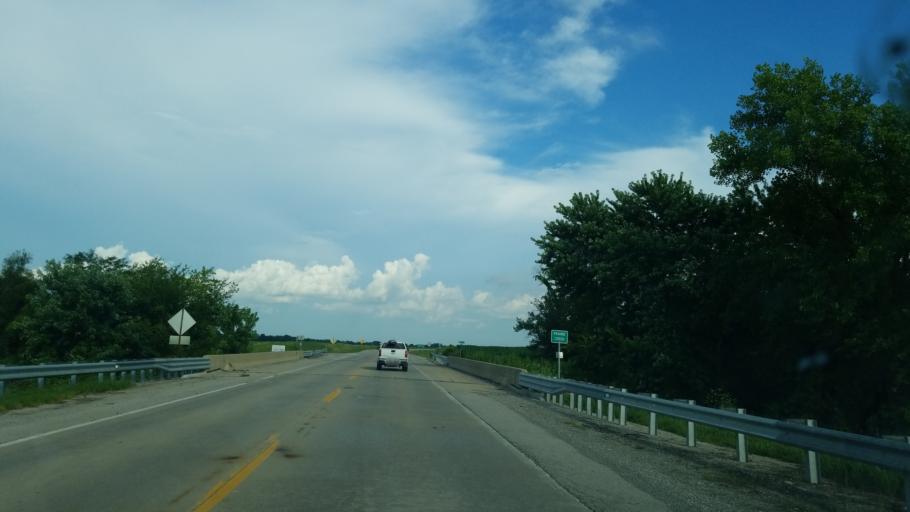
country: US
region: Illinois
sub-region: Marion County
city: Sandoval
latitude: 38.6052
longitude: -89.1136
